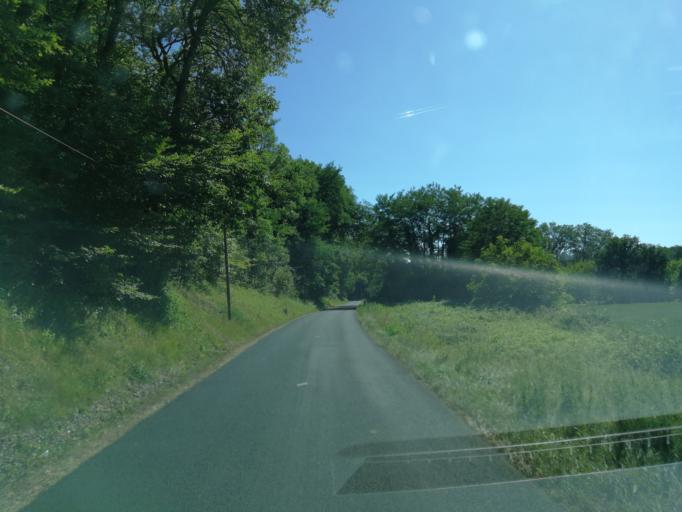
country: FR
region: Aquitaine
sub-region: Departement de la Dordogne
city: Eyvigues-et-Eybenes
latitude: 44.8726
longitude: 1.3833
